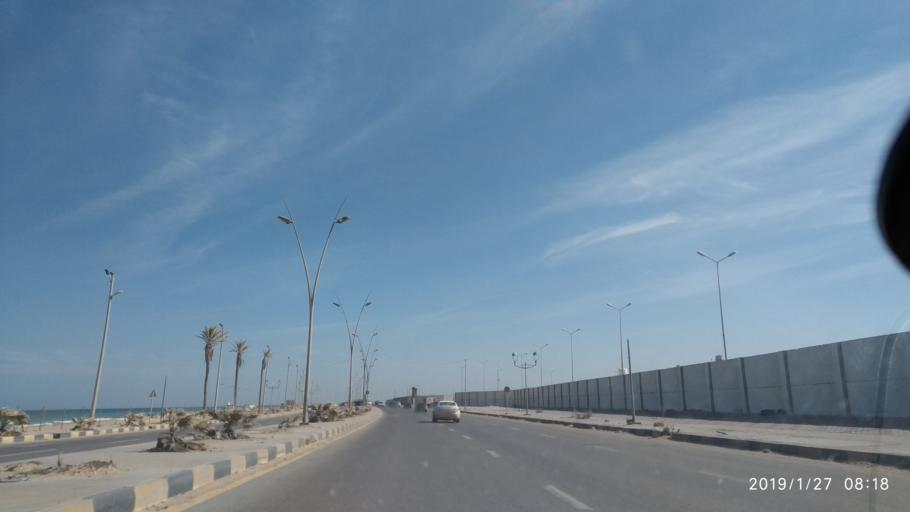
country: LY
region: Tripoli
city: Tagiura
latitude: 32.9083
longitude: 13.2814
